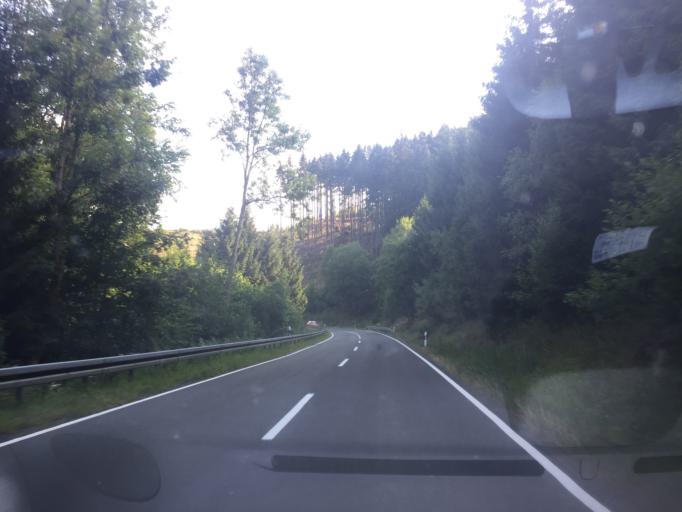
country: DE
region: Saxony-Anhalt
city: Darlingerode
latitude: 51.7915
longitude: 10.7383
